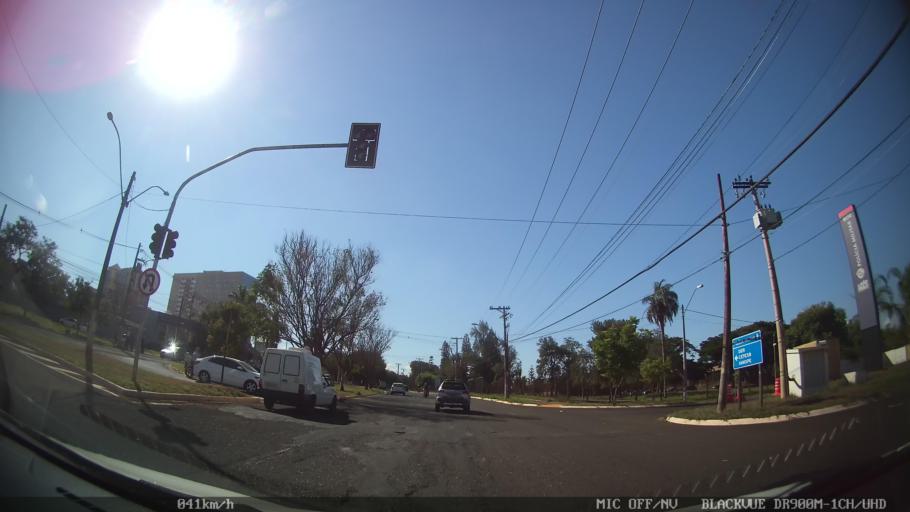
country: BR
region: Sao Paulo
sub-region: Ribeirao Preto
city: Ribeirao Preto
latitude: -21.2032
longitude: -47.7680
